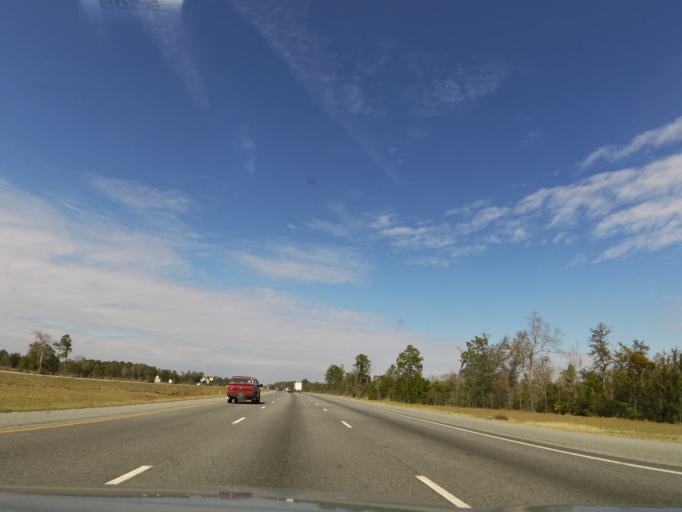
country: US
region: Georgia
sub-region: McIntosh County
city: Darien
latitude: 31.4206
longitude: -81.4431
